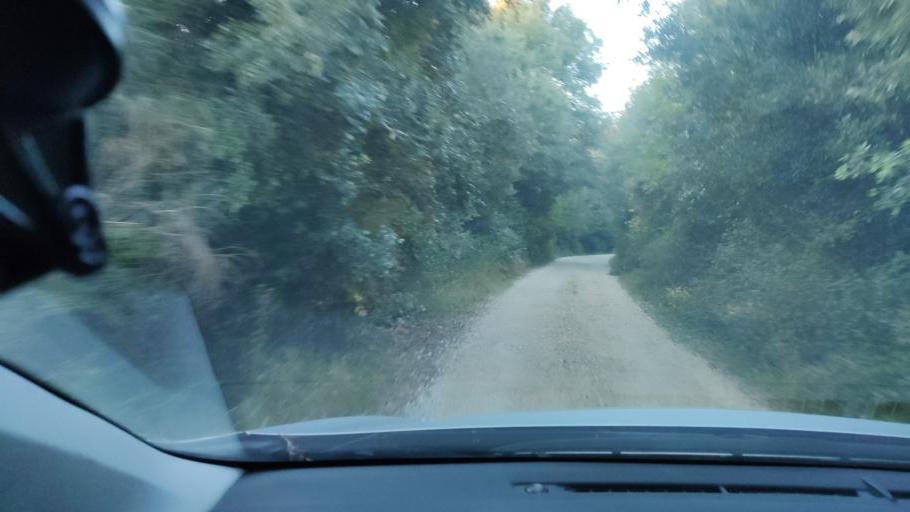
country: IT
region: Umbria
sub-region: Provincia di Terni
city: Amelia
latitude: 42.5817
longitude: 12.4344
